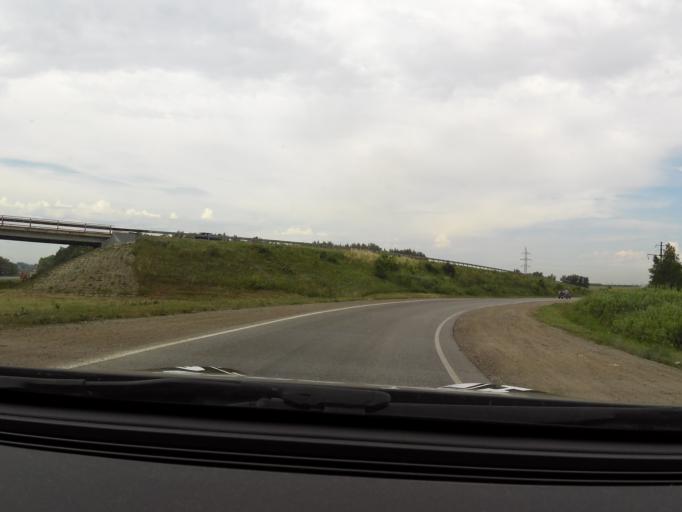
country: RU
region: Bashkortostan
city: Iglino
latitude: 54.7431
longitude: 56.3050
